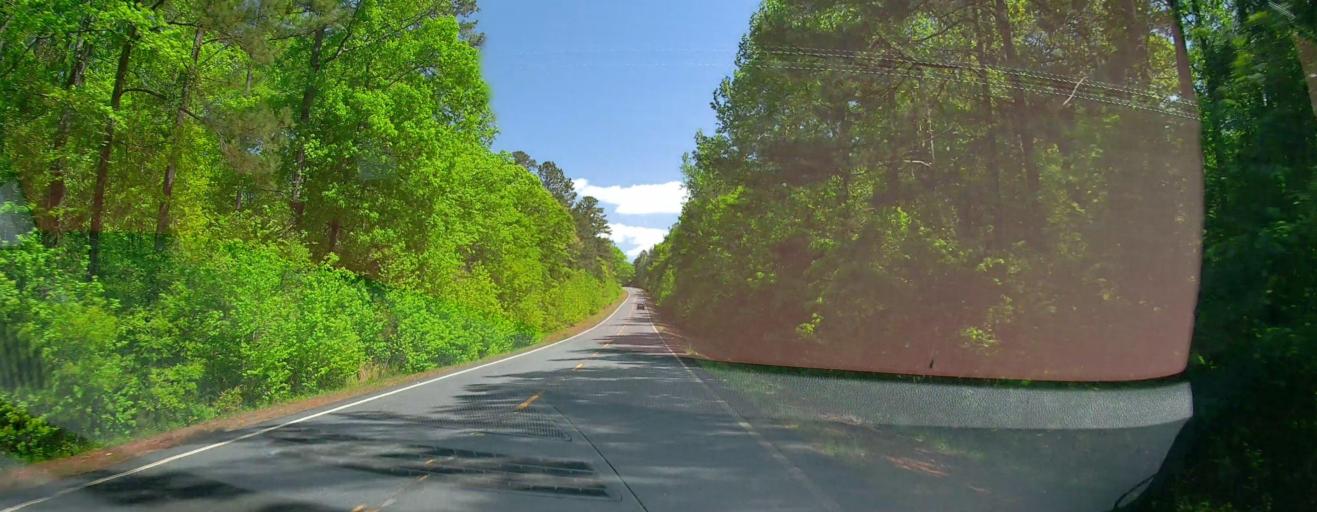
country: US
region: Georgia
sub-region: Putnam County
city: Eatonton
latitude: 33.2115
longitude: -83.4791
